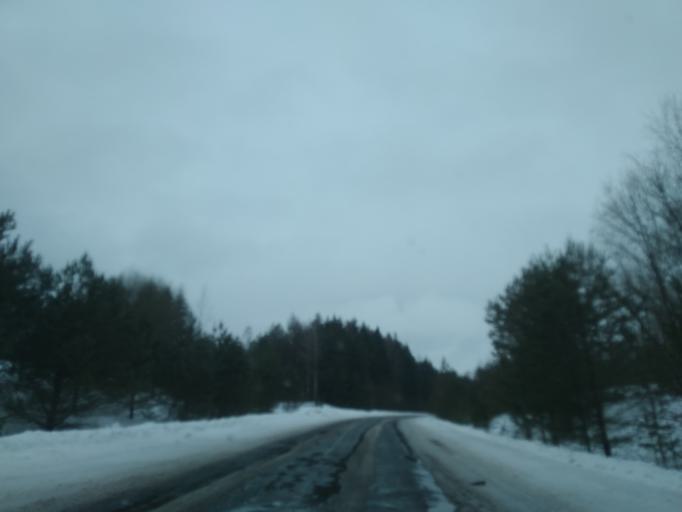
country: BY
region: Minsk
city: Ivyanyets
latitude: 53.8457
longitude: 26.7926
